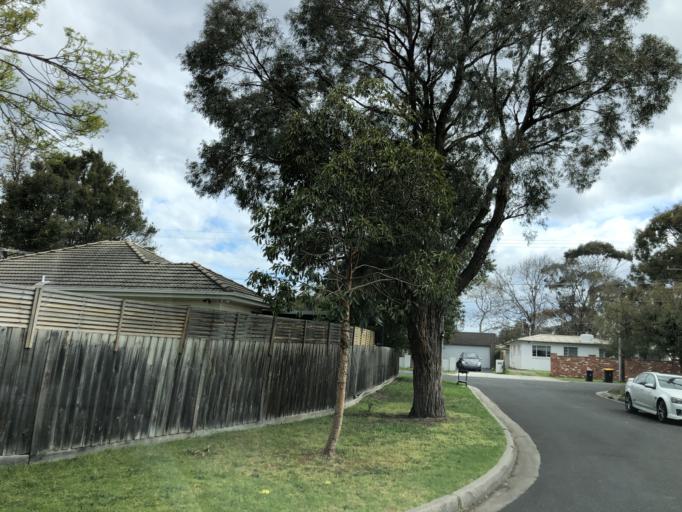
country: AU
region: Victoria
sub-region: Kingston
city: Carrum
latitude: -38.0738
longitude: 145.1324
